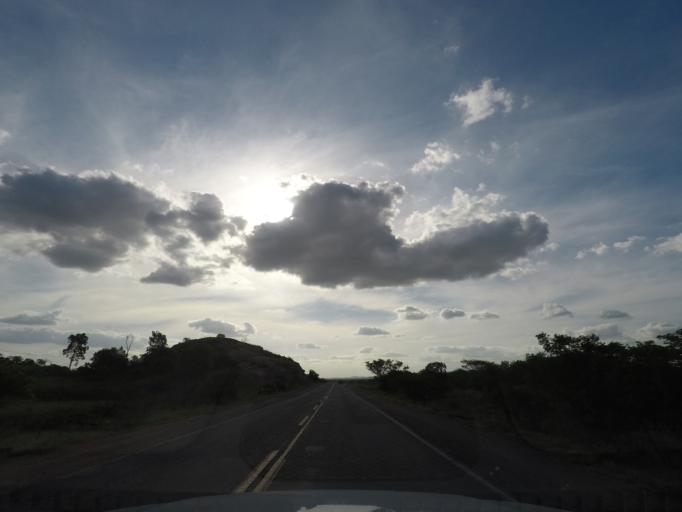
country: BR
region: Bahia
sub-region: Anguera
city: Anguera
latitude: -12.1837
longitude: -39.4697
